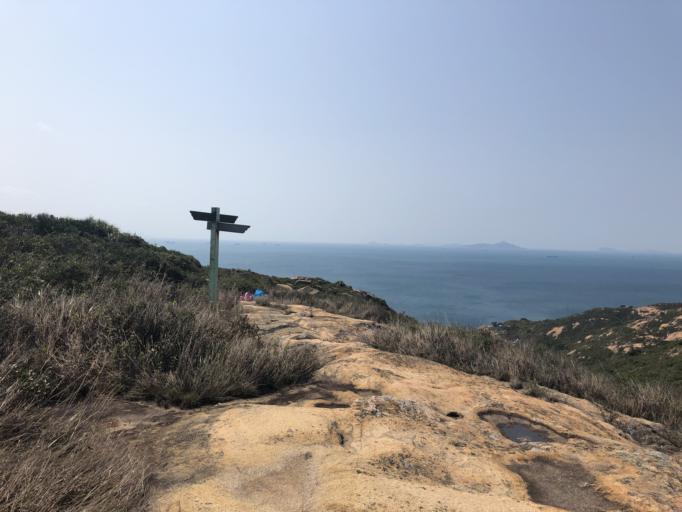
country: HK
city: Sok Kwu Wan
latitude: 22.1672
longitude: 114.2610
